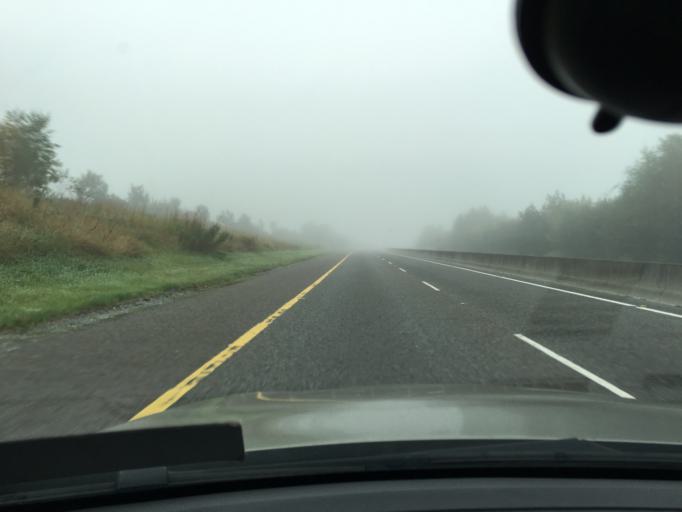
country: IE
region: Leinster
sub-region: An Iarmhi
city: Rochfortbridge
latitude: 53.3773
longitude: -7.3829
